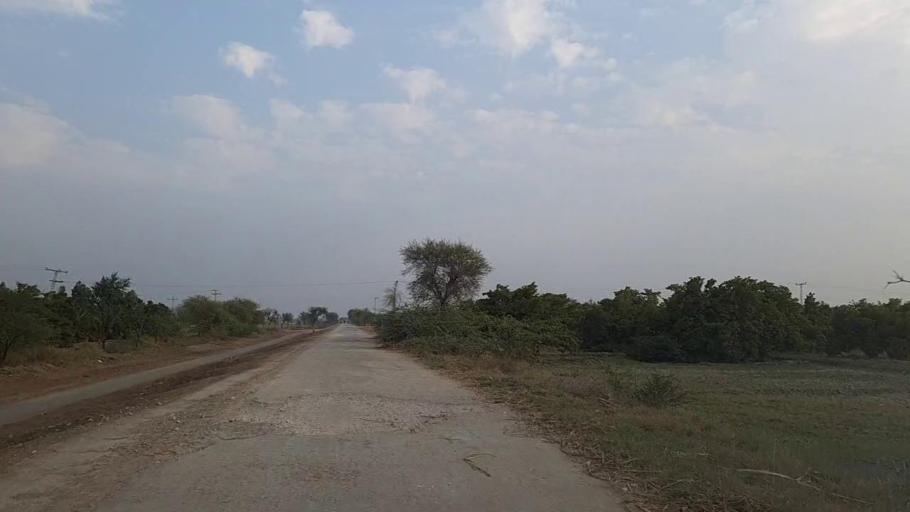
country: PK
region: Sindh
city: Mirwah Gorchani
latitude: 25.2996
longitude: 69.2215
